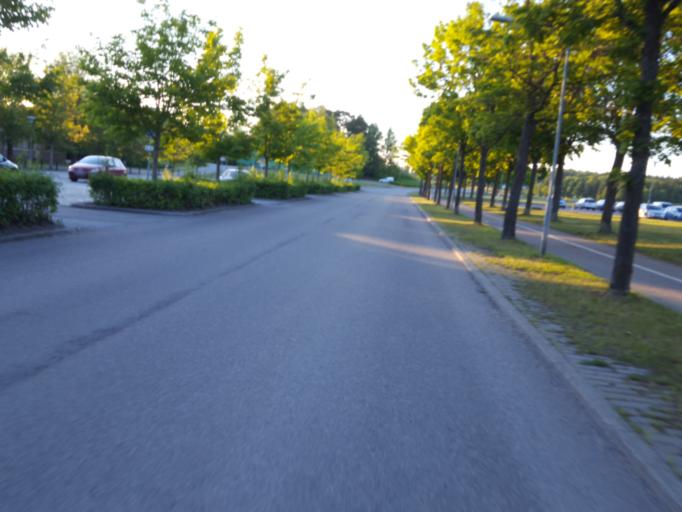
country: SE
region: Uppsala
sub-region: Uppsala Kommun
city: Uppsala
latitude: 59.8207
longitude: 17.6567
